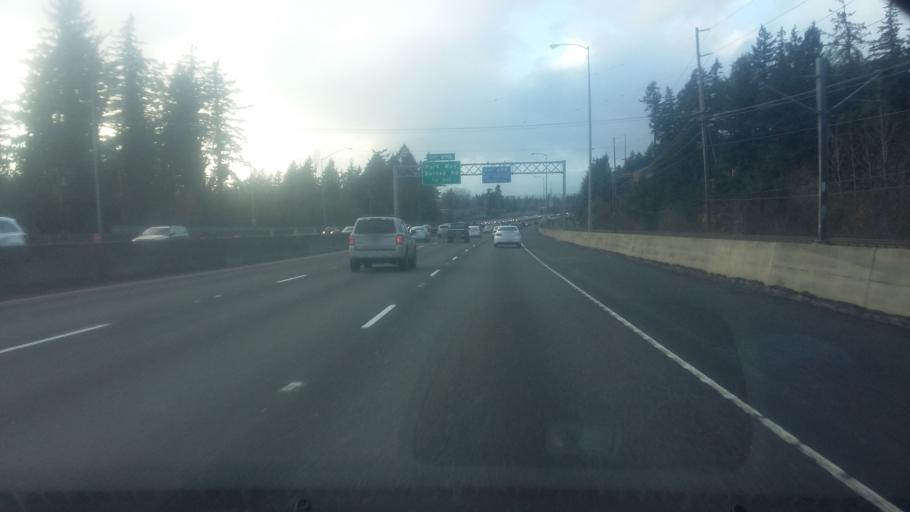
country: US
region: Oregon
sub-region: Washington County
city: West Slope
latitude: 45.5059
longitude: -122.7641
